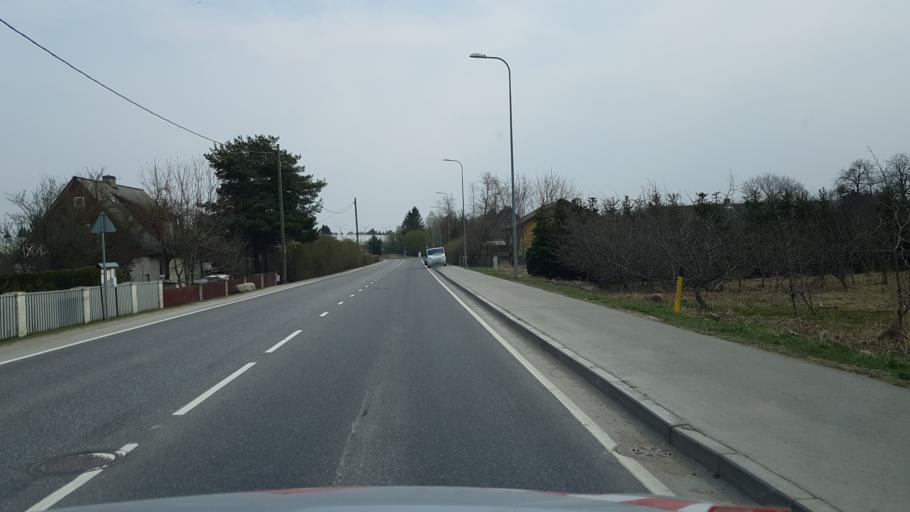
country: EE
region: Harju
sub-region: Rae vald
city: Jueri
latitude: 59.3792
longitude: 24.8397
